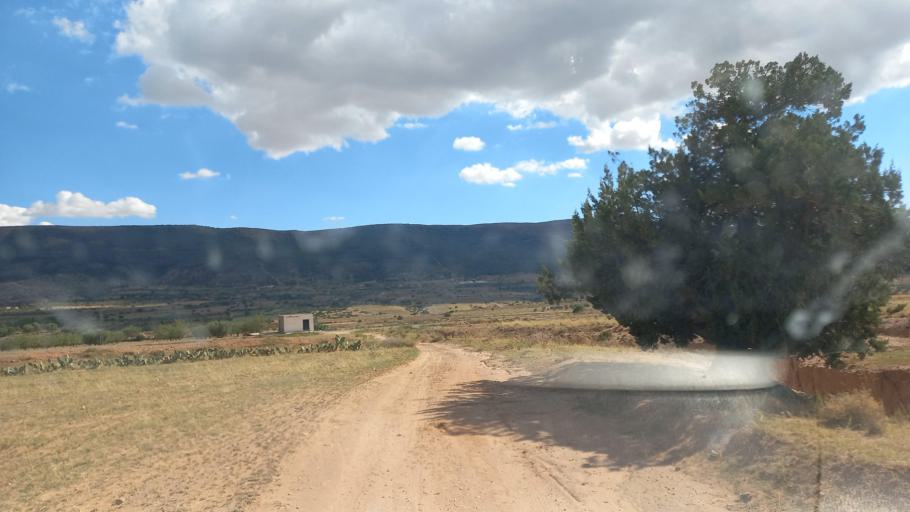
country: TN
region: Al Qasrayn
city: Kasserine
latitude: 35.3703
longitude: 8.8848
